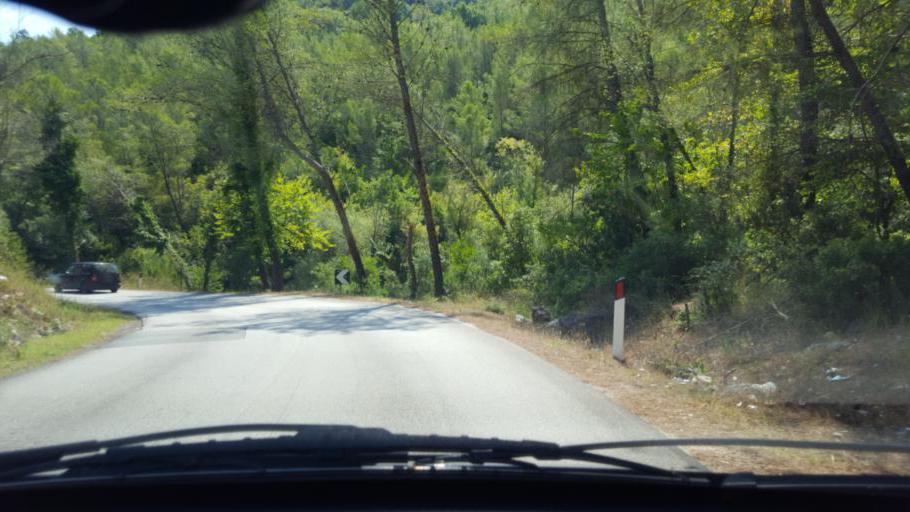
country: AL
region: Vlore
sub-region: Rrethi i Delvines
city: Mesopotam
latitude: 39.9207
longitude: 20.1534
